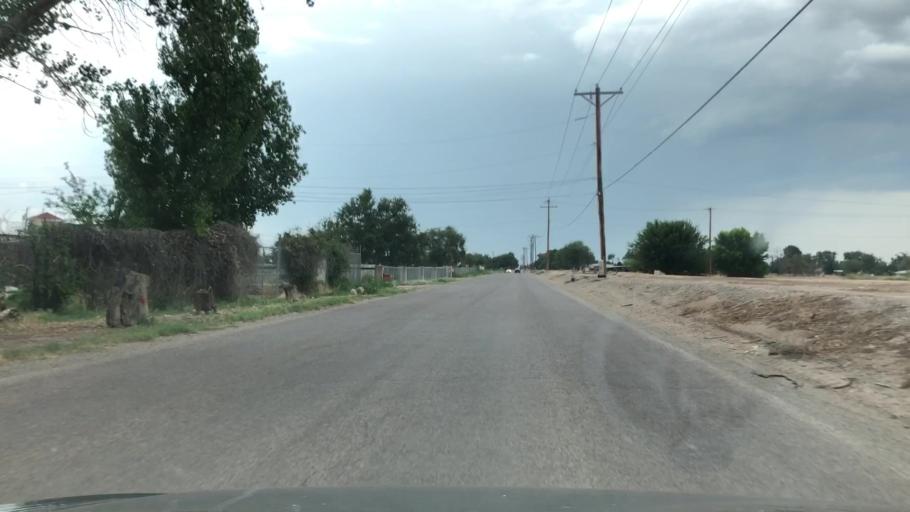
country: US
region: Texas
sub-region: El Paso County
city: Canutillo
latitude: 31.9139
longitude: -106.6248
